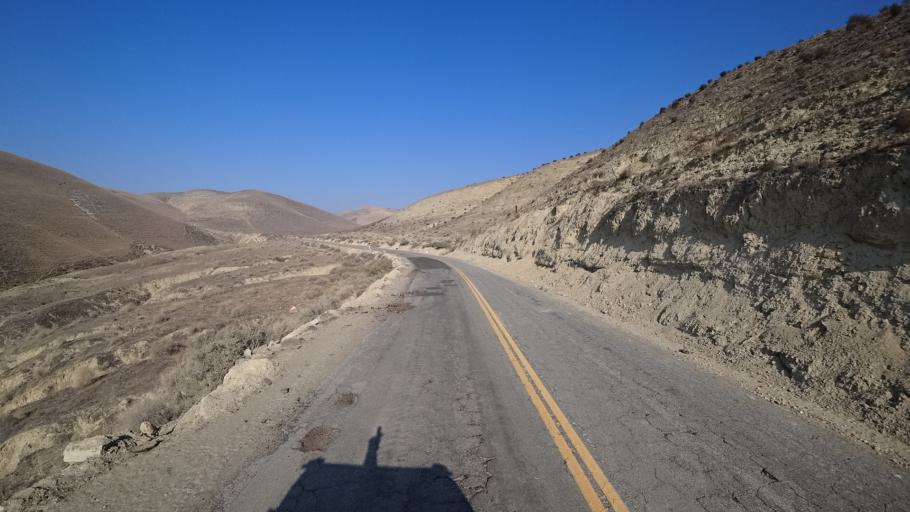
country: US
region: California
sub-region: Kern County
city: Oildale
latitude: 35.4421
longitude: -118.8264
